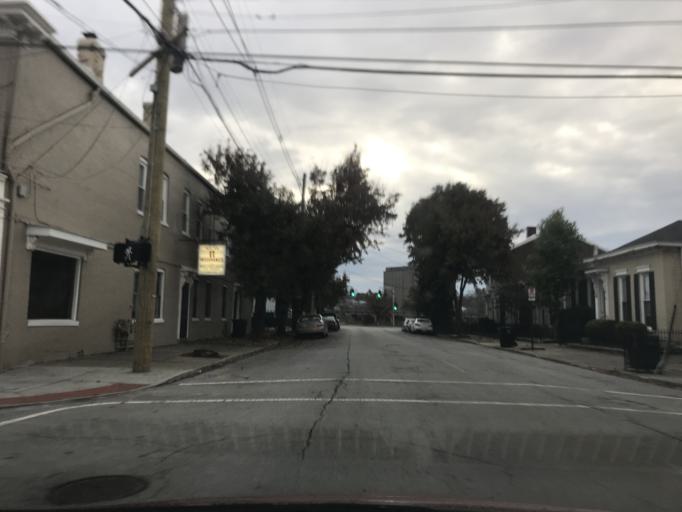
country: US
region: Kentucky
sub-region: Jefferson County
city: Louisville
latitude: 38.2467
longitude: -85.7372
